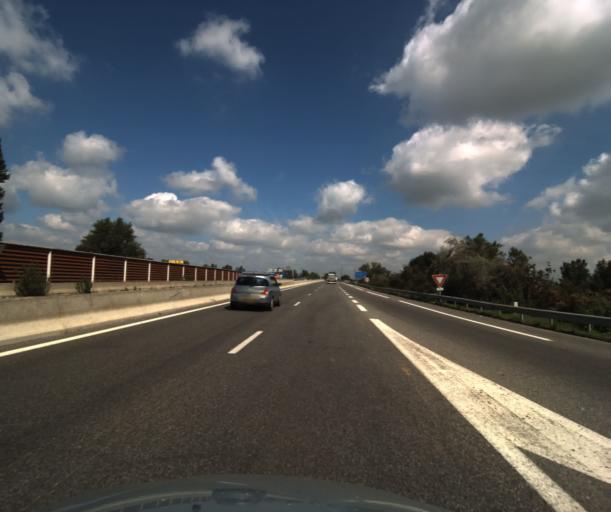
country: FR
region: Midi-Pyrenees
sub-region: Departement de la Haute-Garonne
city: Pinsaguel
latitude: 43.5150
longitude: 1.3796
